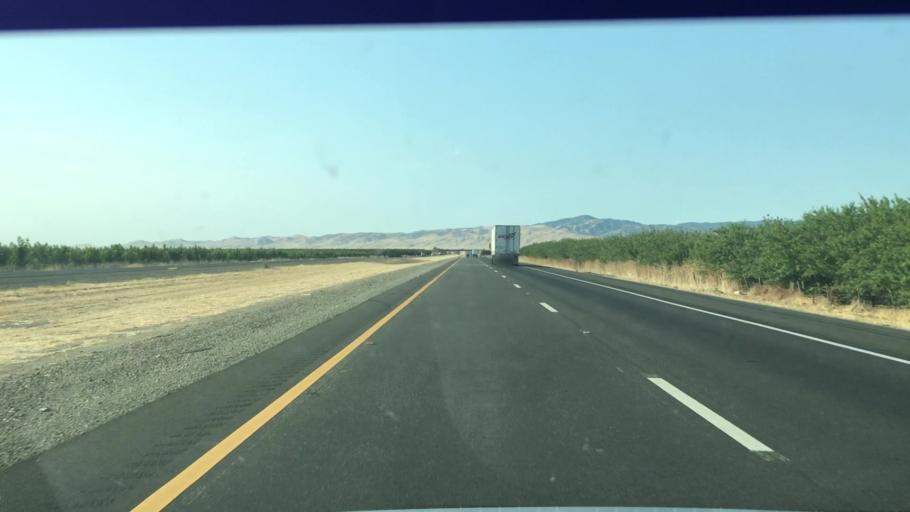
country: US
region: California
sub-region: San Joaquin County
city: Tracy
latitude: 37.7090
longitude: -121.3436
